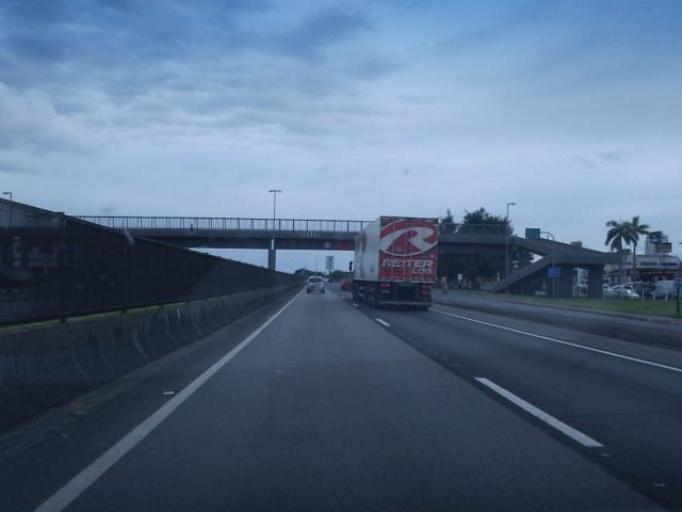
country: BR
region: Sao Paulo
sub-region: Registro
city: Registro
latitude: -24.5003
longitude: -47.8449
